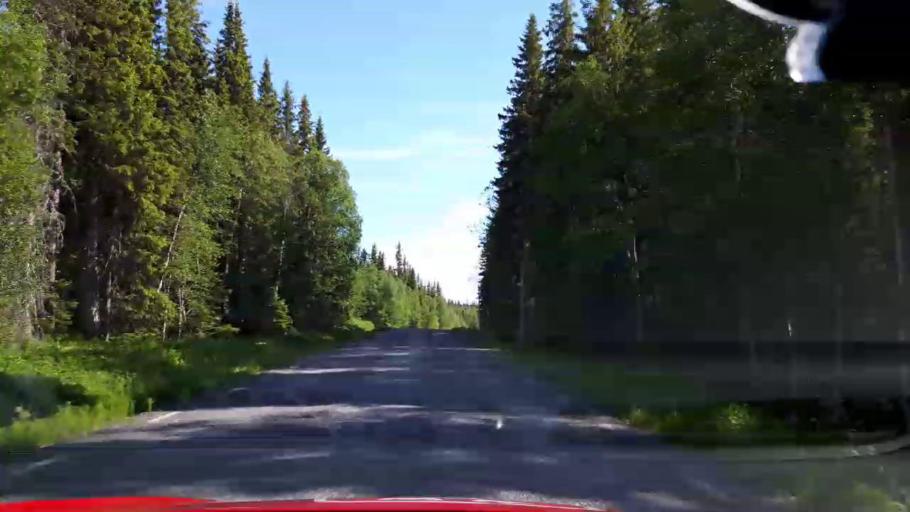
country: SE
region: Jaemtland
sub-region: Krokoms Kommun
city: Valla
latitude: 63.7459
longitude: 14.1186
